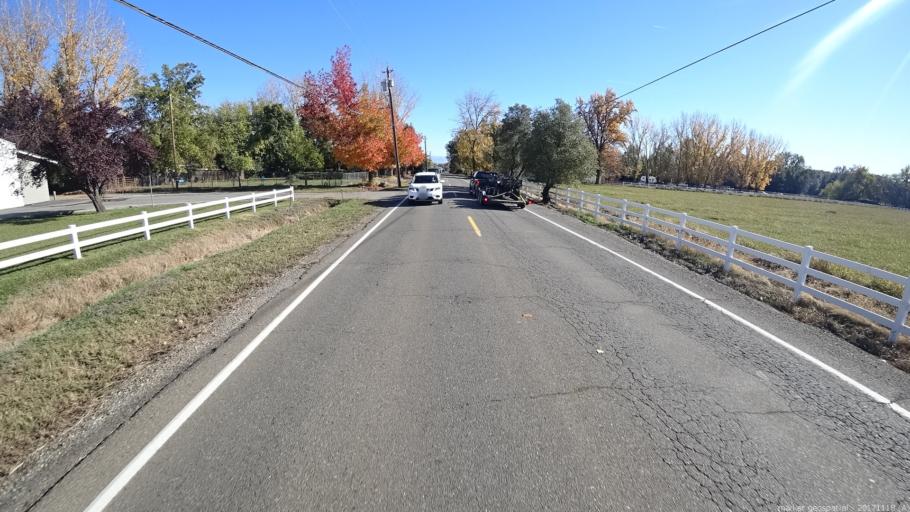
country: US
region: California
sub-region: Shasta County
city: Cottonwood
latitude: 40.3893
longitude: -122.2964
